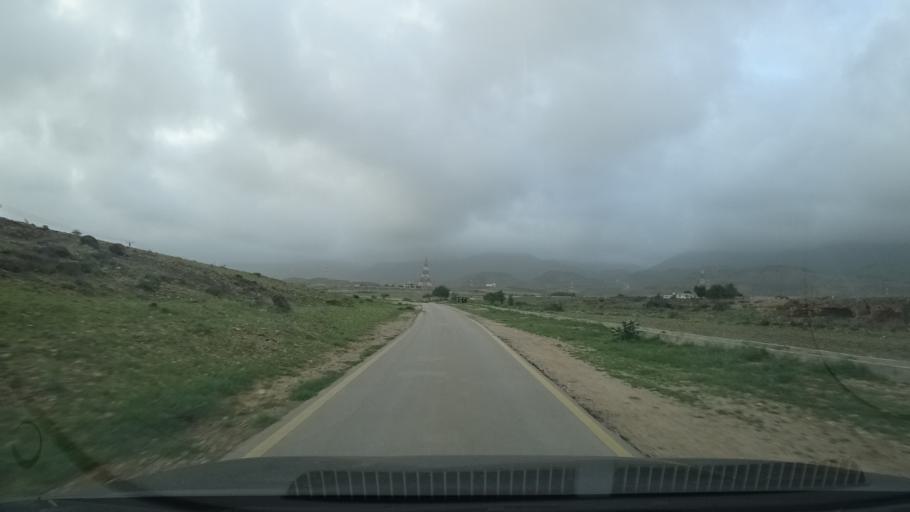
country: OM
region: Zufar
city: Salalah
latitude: 17.0979
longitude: 54.2332
